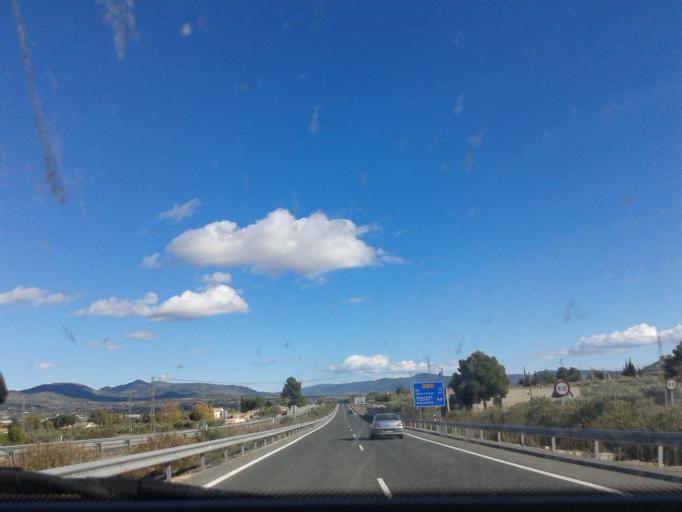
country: ES
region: Valencia
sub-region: Provincia de Alicante
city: Castalla
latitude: 38.6062
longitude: -0.7049
